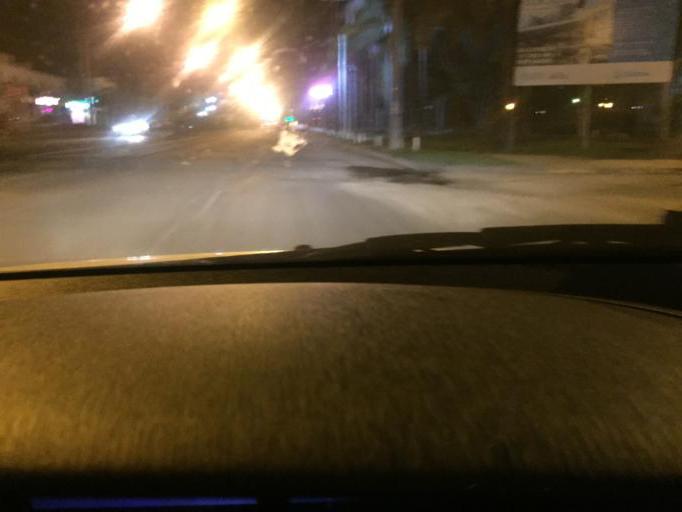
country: AR
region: Cordoba
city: Villa Allende
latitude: -31.3074
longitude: -64.2809
